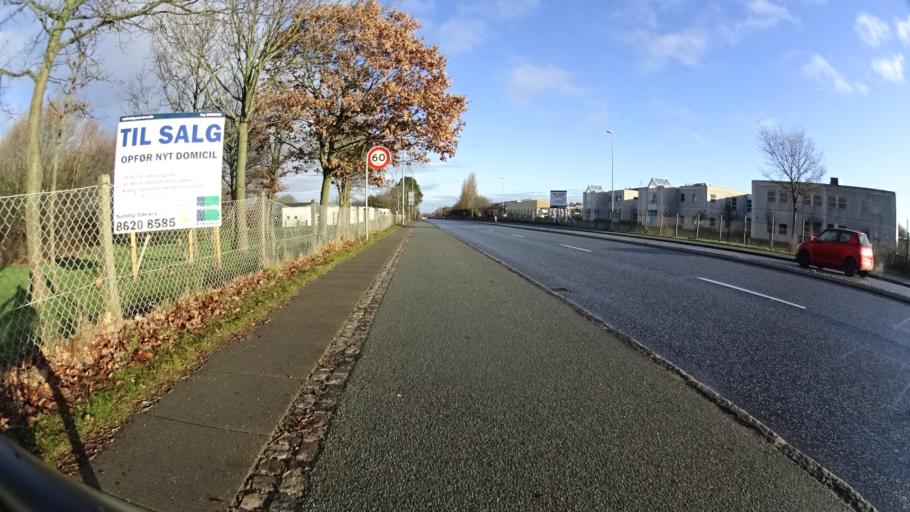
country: DK
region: Central Jutland
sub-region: Arhus Kommune
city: Tranbjerg
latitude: 56.1064
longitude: 10.1458
